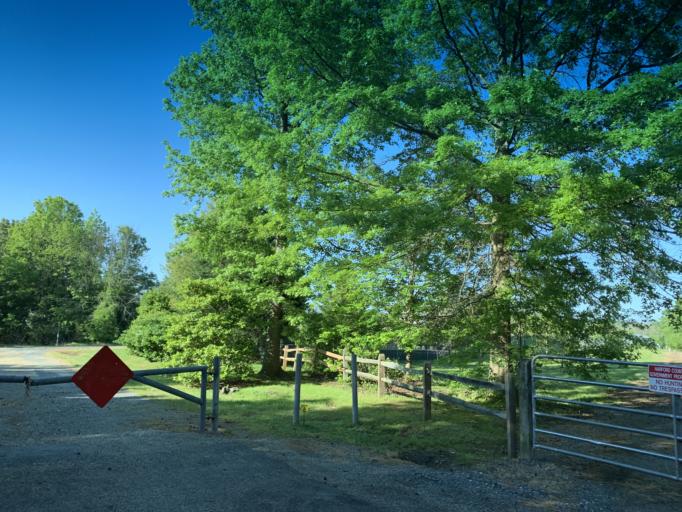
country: US
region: Maryland
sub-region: Harford County
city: Riverside
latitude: 39.4665
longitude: -76.2639
